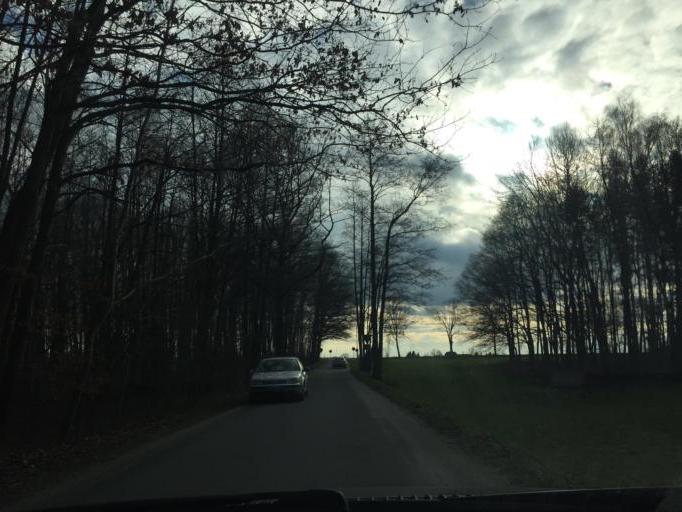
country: DE
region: Saxony
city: Ebersbach
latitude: 51.2087
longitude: 13.6722
